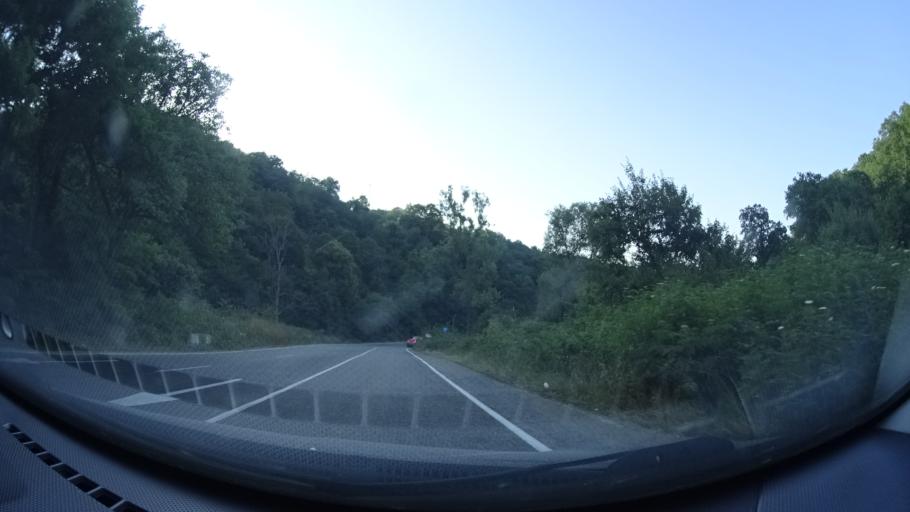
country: GE
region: Kakheti
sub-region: Gurjaani
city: Gurjaani
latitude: 41.6699
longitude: 45.8365
